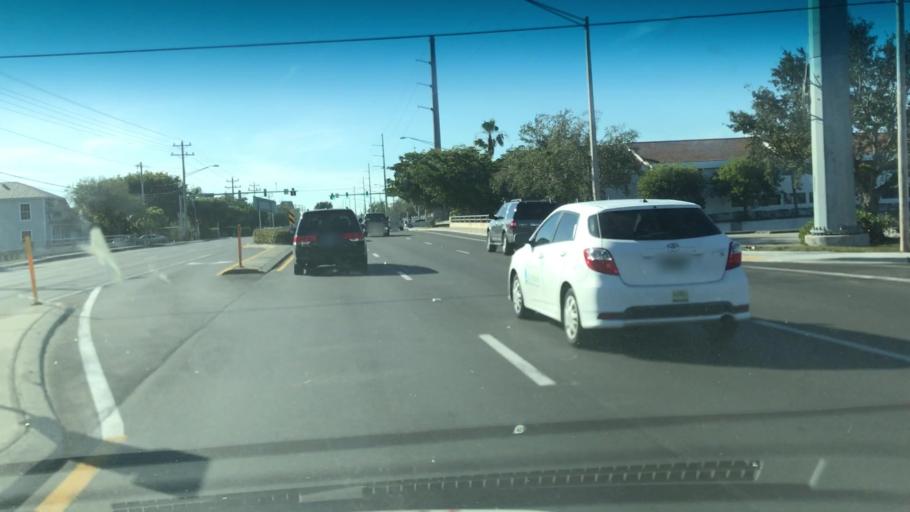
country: US
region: Florida
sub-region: Lee County
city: Cape Coral
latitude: 26.6005
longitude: -81.9415
